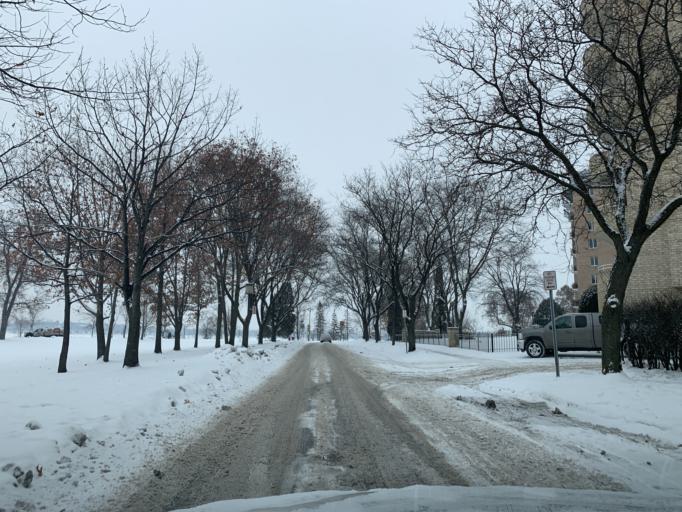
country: US
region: Minnesota
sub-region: Hennepin County
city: Saint Louis Park
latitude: 44.9456
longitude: -93.3206
